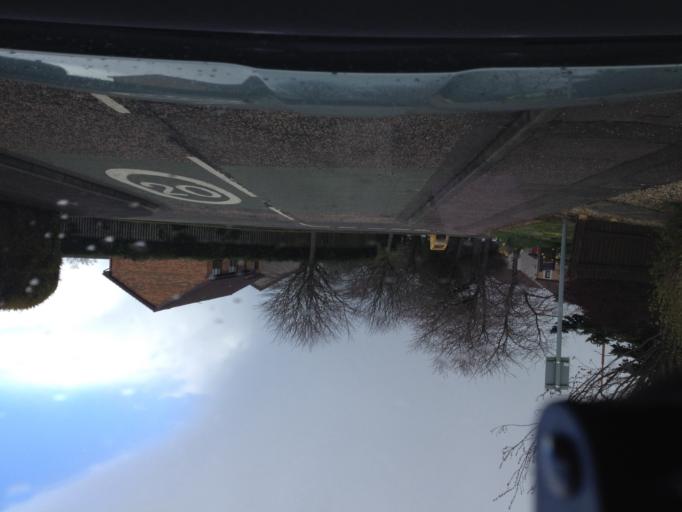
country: GB
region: Scotland
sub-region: West Lothian
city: Linlithgow
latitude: 55.9817
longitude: -3.5748
